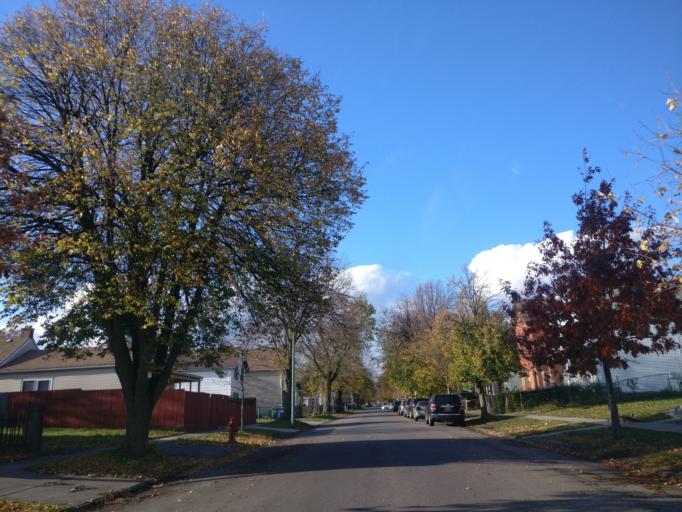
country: US
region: New York
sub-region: Erie County
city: Buffalo
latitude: 42.8966
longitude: -78.8894
